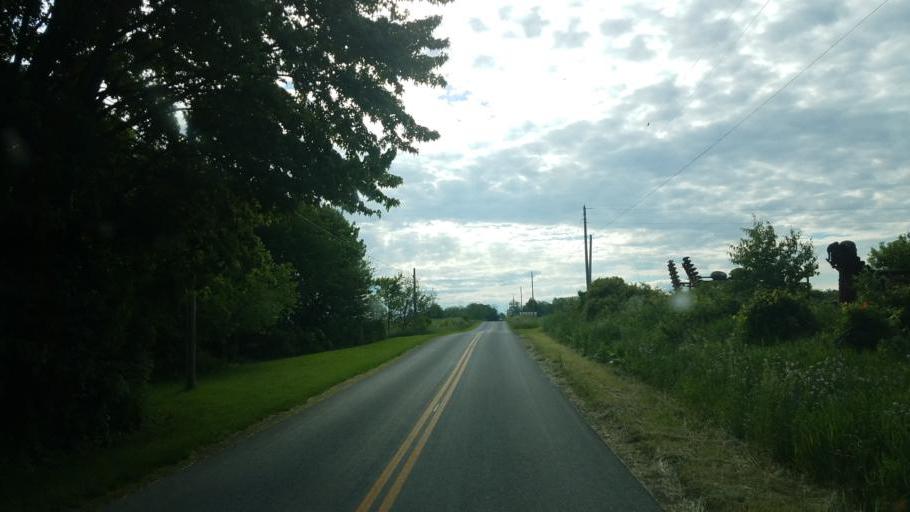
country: US
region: Ohio
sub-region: Medina County
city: Westfield Center
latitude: 40.9878
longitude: -81.9686
